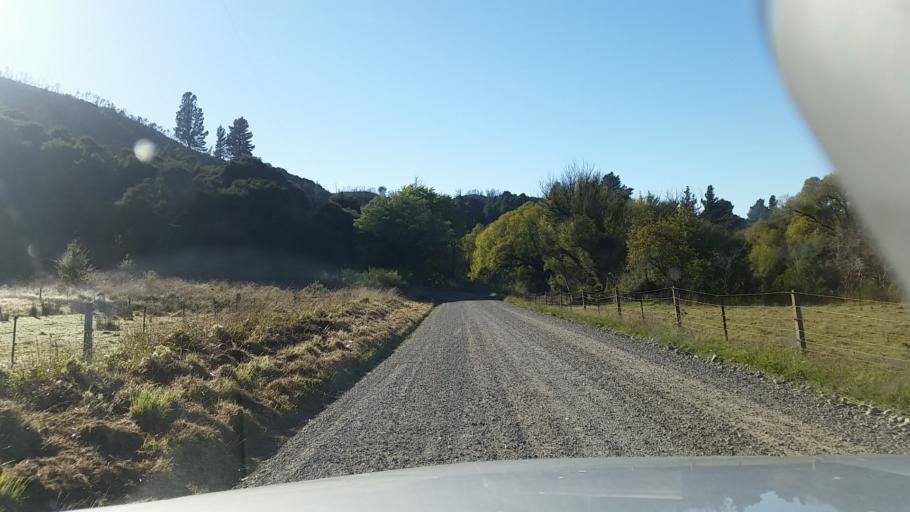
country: NZ
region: Marlborough
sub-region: Marlborough District
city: Blenheim
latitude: -41.4444
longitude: 173.8872
